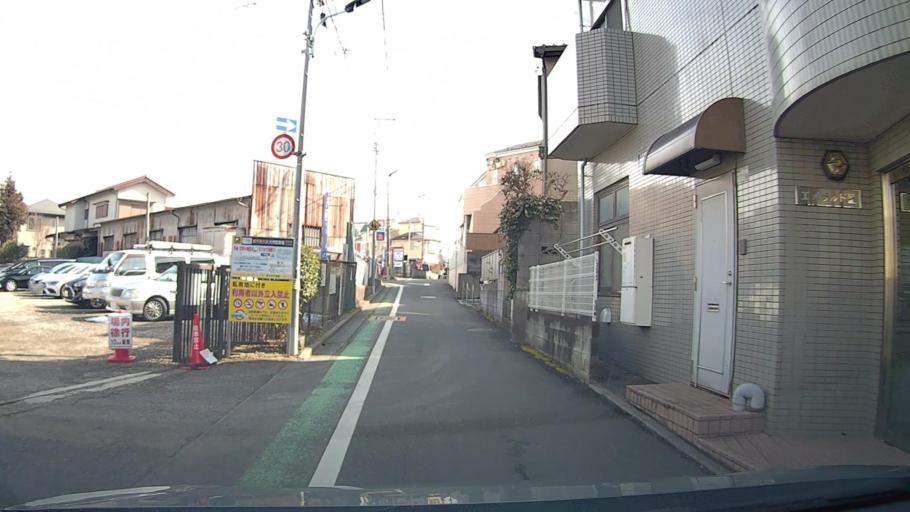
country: JP
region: Tokyo
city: Musashino
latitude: 35.7423
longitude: 139.5742
